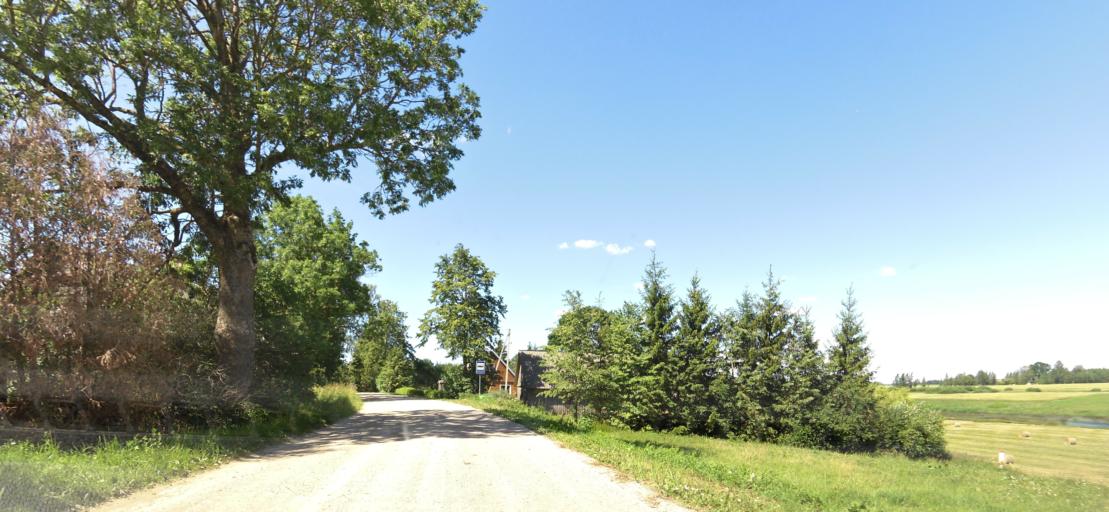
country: LV
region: Bauskas Rajons
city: Bauska
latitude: 56.2766
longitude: 24.3522
